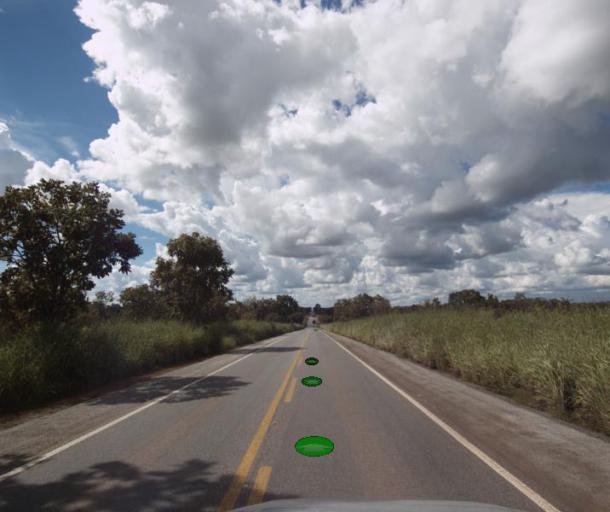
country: BR
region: Goias
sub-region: Porangatu
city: Porangatu
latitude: -13.3795
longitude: -49.1272
